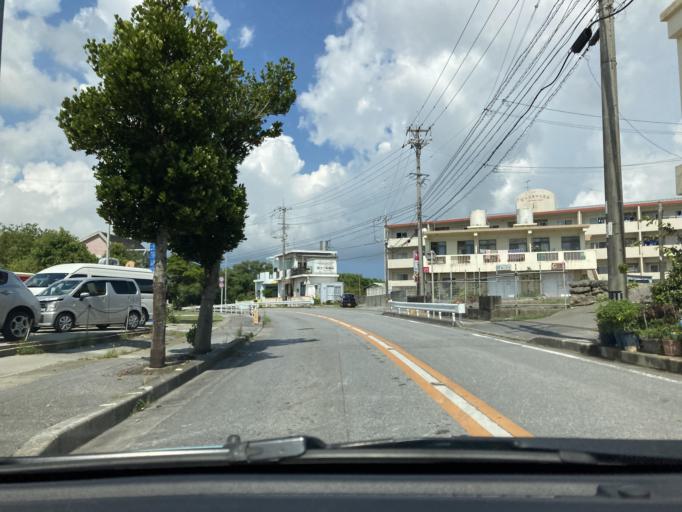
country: JP
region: Okinawa
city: Tomigusuku
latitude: 26.1606
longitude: 127.7447
